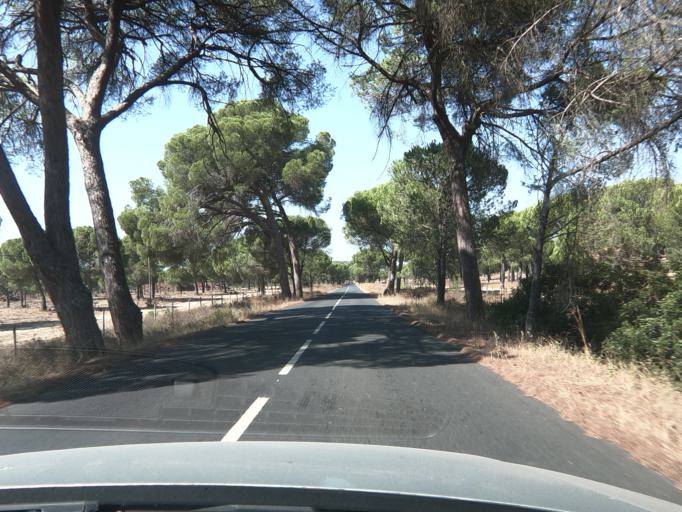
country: PT
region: Setubal
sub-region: Alcacer do Sal
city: Alcacer do Sal
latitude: 38.3440
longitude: -8.4519
